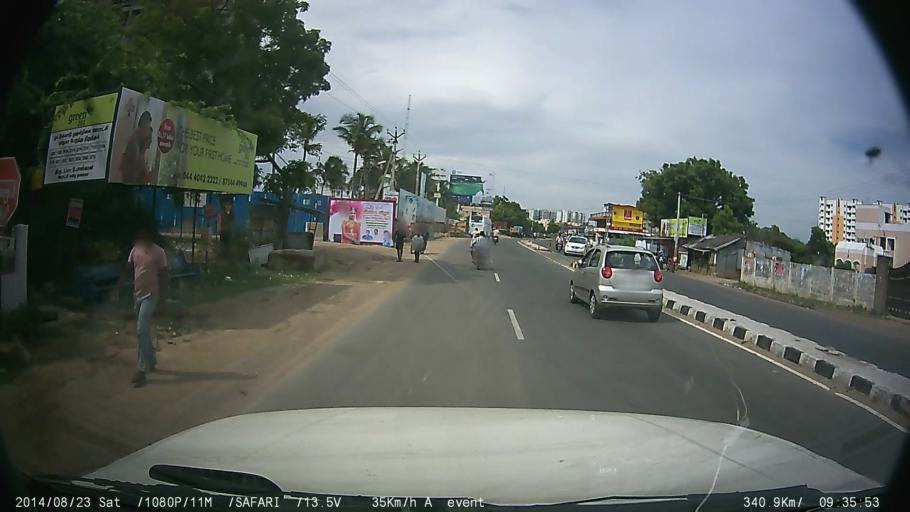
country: IN
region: Tamil Nadu
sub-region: Kancheepuram
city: Vengavasal
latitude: 12.8104
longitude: 80.2279
